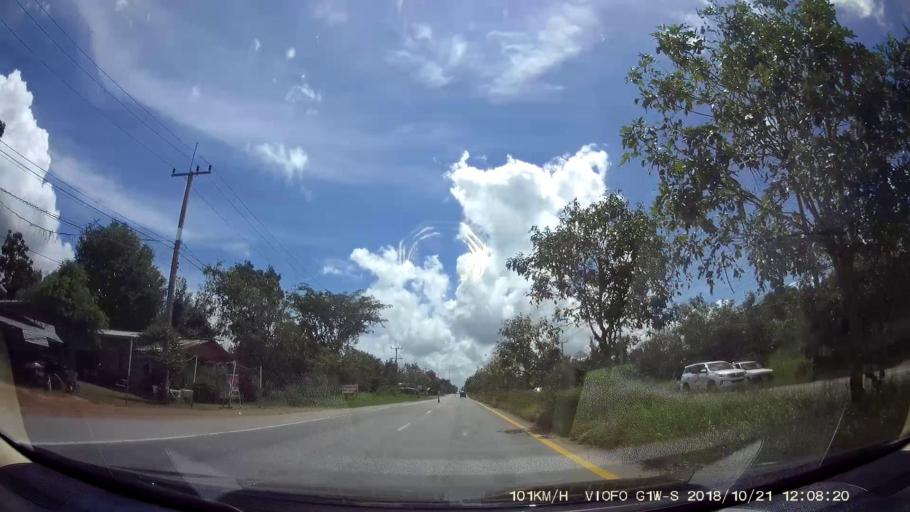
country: TH
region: Chaiyaphum
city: Chatturat
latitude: 15.4351
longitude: 101.8303
